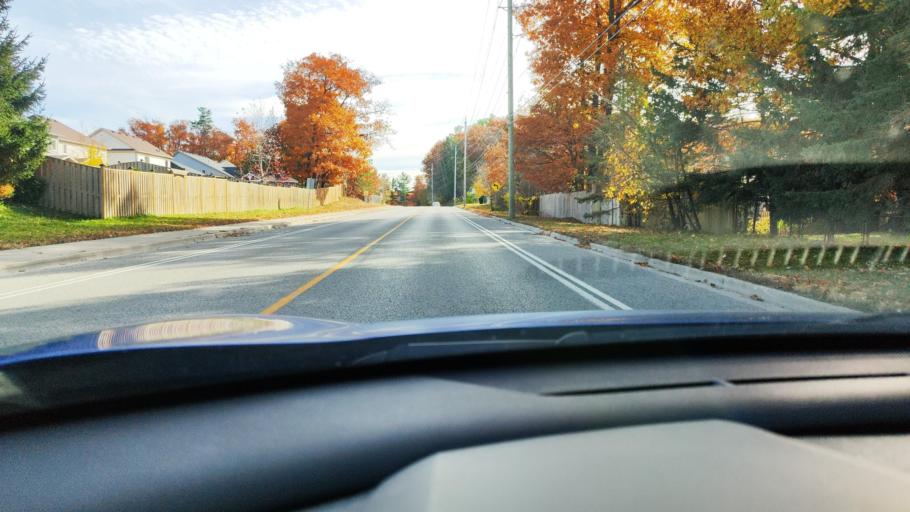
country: CA
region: Ontario
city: Wasaga Beach
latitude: 44.5209
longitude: -79.9971
